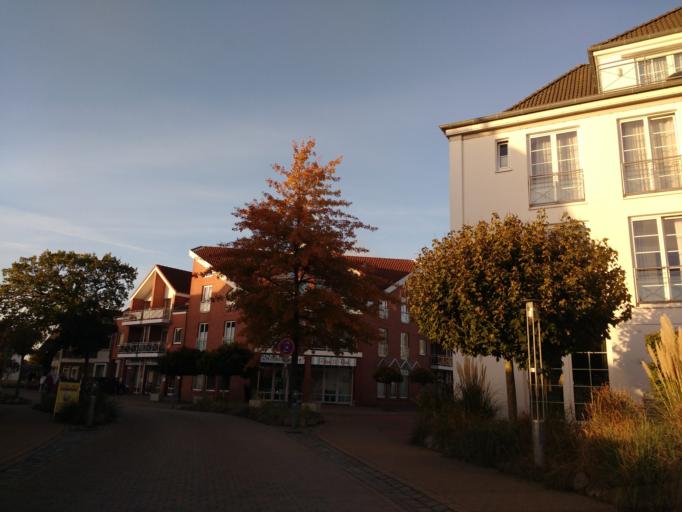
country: DE
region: Schleswig-Holstein
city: Kellenhusen
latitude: 54.1888
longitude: 11.0596
